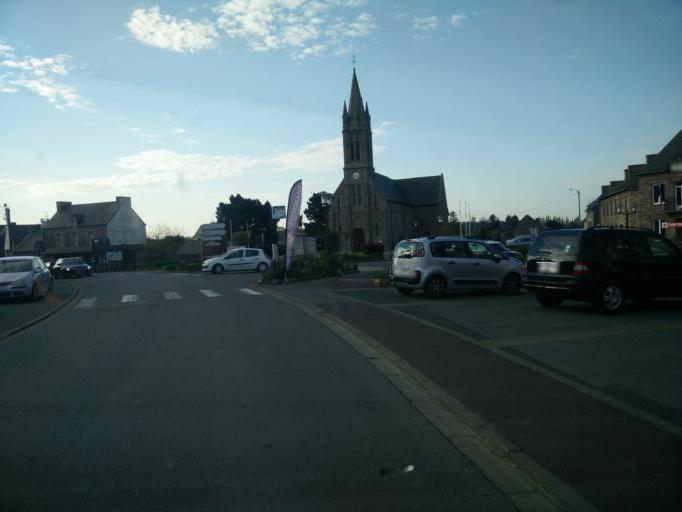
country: FR
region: Brittany
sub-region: Departement des Cotes-d'Armor
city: Plurien
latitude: 48.6284
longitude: -2.3654
